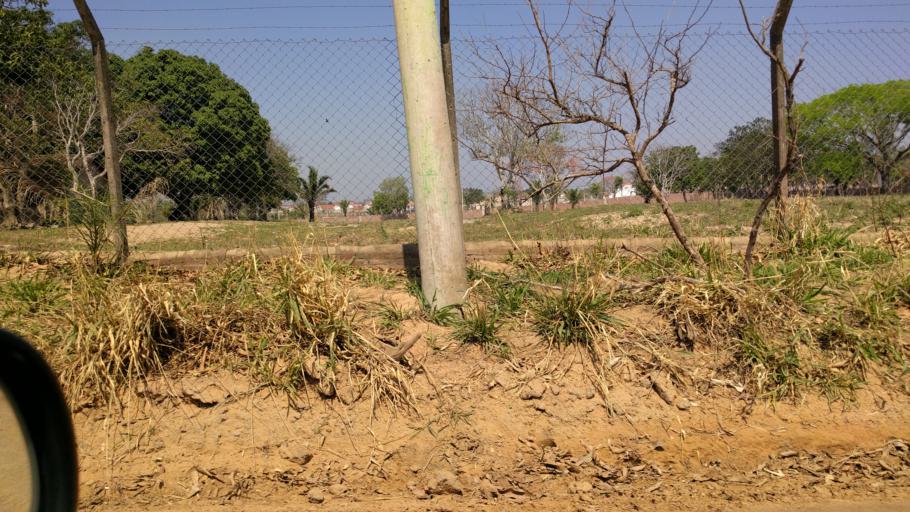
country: BO
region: Santa Cruz
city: Santa Cruz de la Sierra
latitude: -17.7562
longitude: -63.2310
